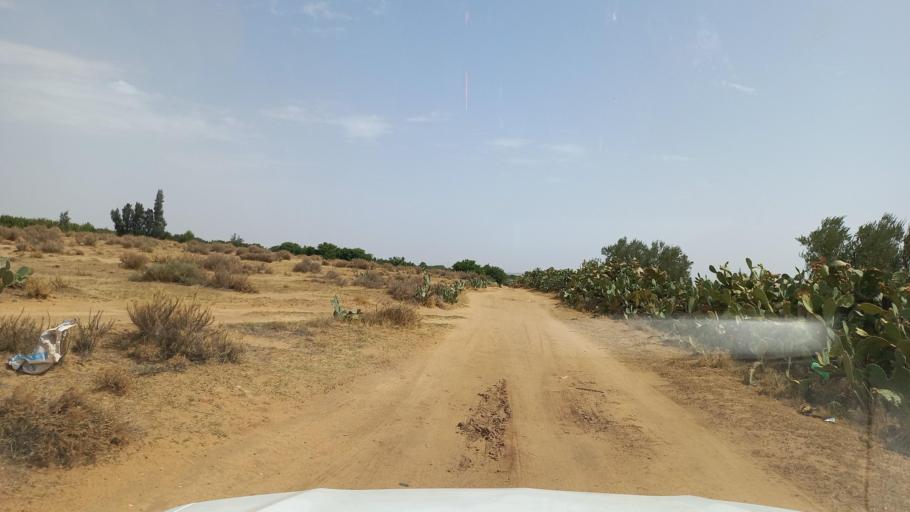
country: TN
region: Al Qasrayn
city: Kasserine
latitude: 35.2454
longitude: 9.0658
